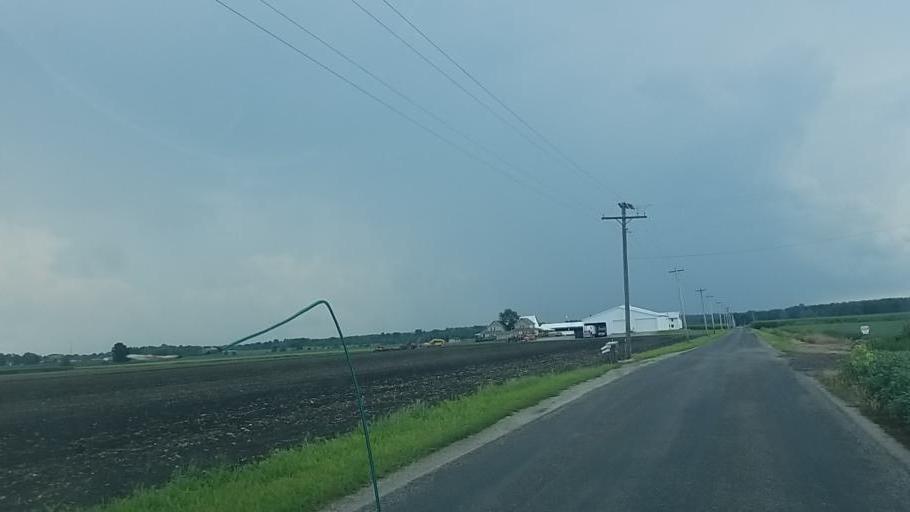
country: US
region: Ohio
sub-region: Medina County
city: Lodi
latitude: 41.0099
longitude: -82.0186
